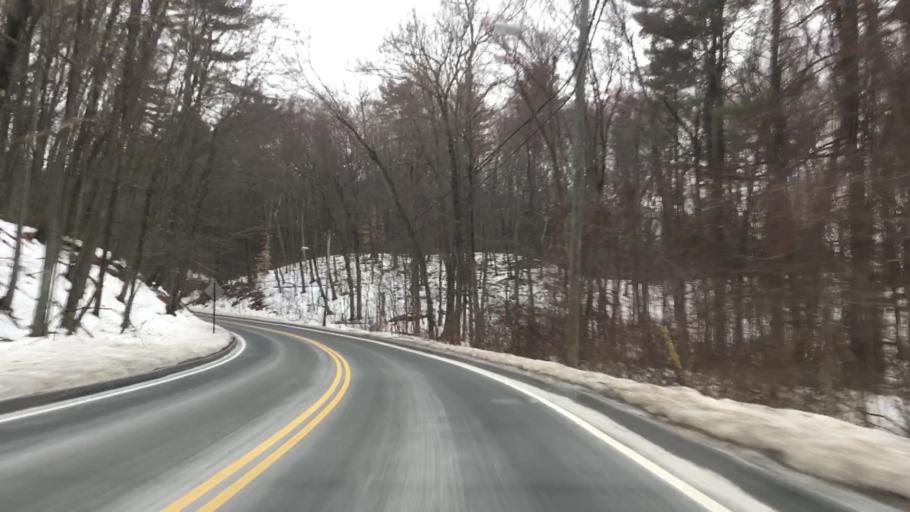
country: US
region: Massachusetts
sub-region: Hampden County
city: West Springfield
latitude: 42.0977
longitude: -72.6831
